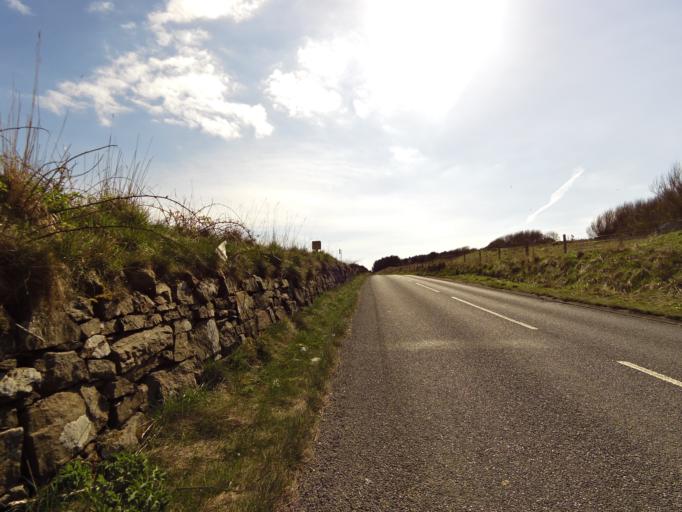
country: GB
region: Scotland
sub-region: Aberdeen City
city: Aberdeen
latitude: 57.1127
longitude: -2.0665
